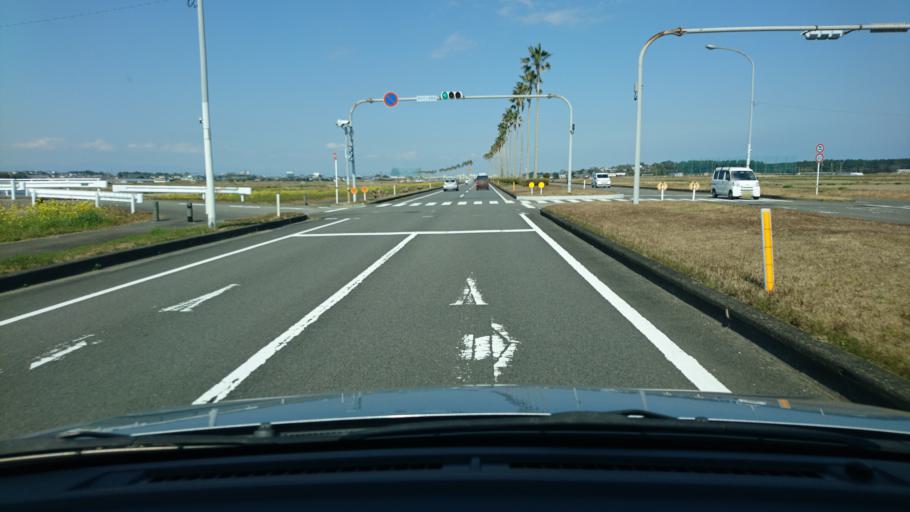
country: JP
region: Miyazaki
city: Miyazaki-shi
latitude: 31.8527
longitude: 131.4433
